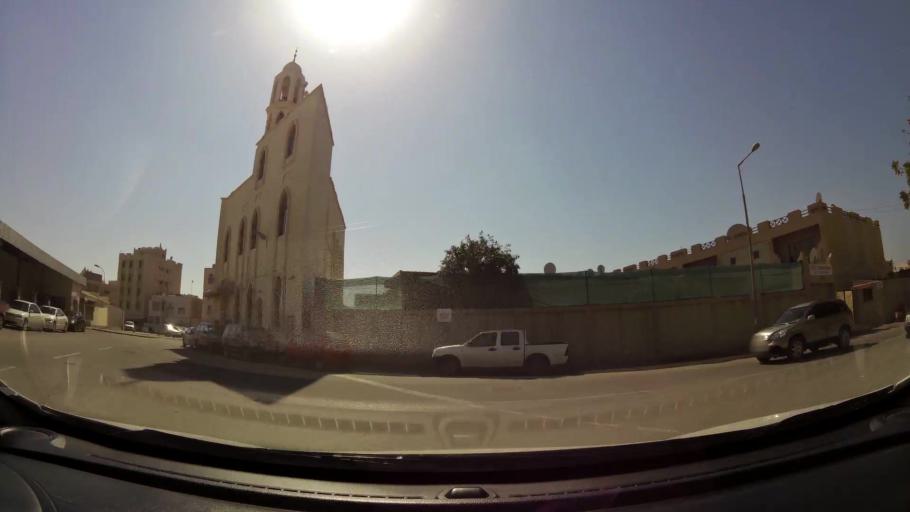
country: BH
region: Manama
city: Manama
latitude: 26.2146
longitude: 50.5686
